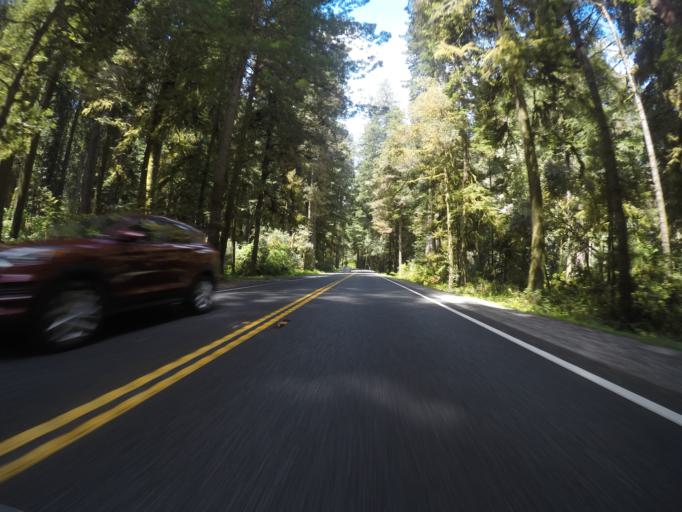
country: US
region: California
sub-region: Del Norte County
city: Bertsch-Oceanview
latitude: 41.8101
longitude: -124.0931
